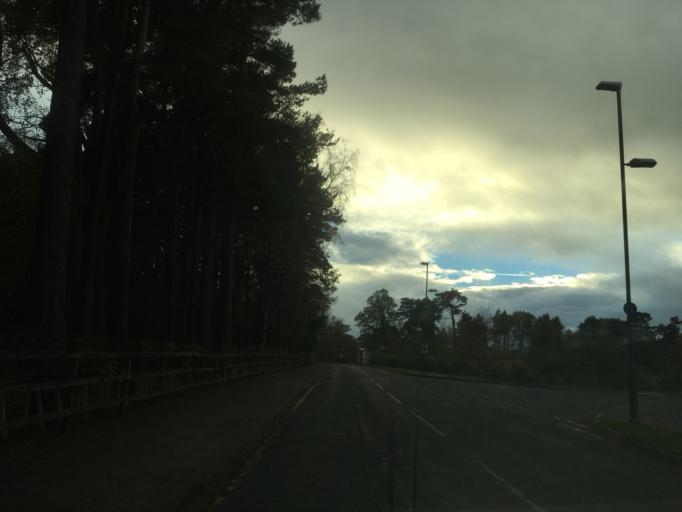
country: GB
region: Scotland
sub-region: Midlothian
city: Penicuik
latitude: 55.8632
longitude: -3.2023
